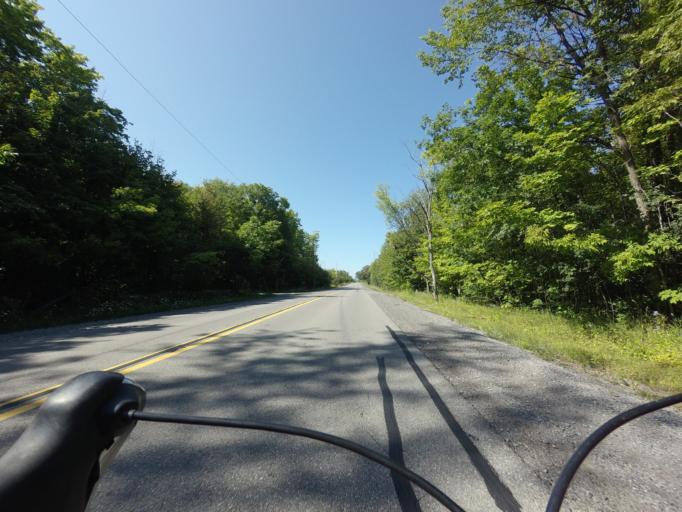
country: CA
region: Ontario
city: Bells Corners
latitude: 45.4234
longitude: -75.9504
